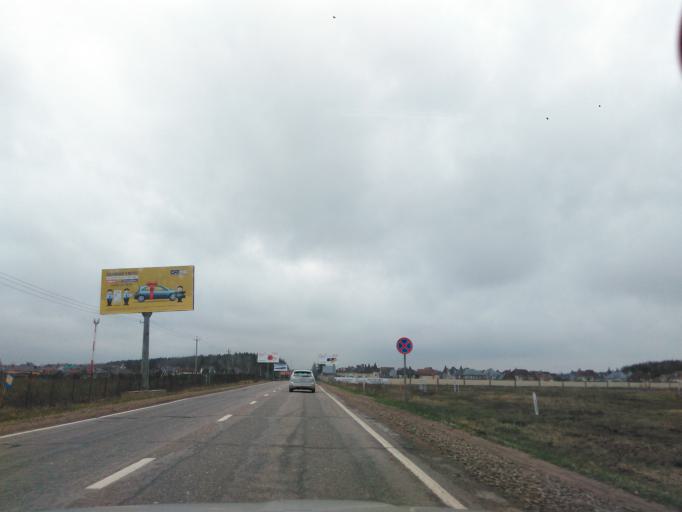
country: RU
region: Moskovskaya
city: Rozhdestveno
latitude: 55.8292
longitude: 37.0336
